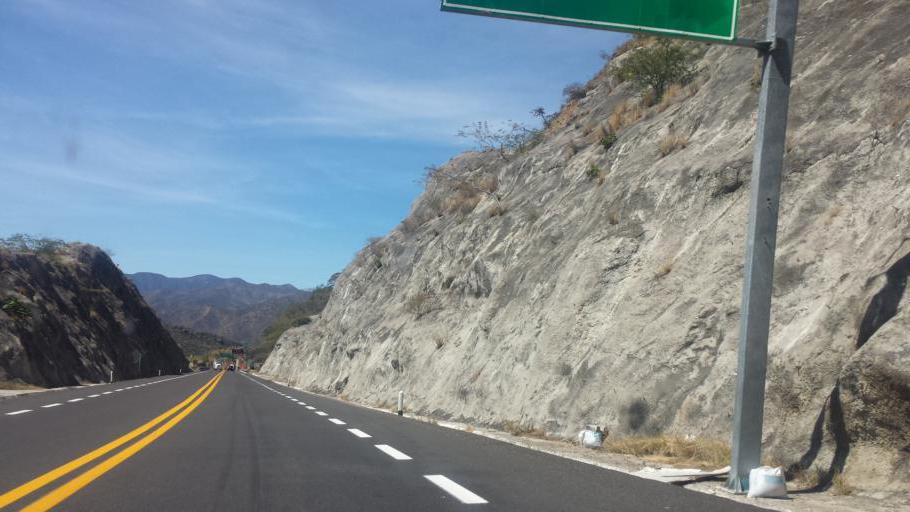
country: MX
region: Puebla
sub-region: San Jose Miahuatlan
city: San Pedro Tetitlan
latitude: 18.1056
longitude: -97.3364
